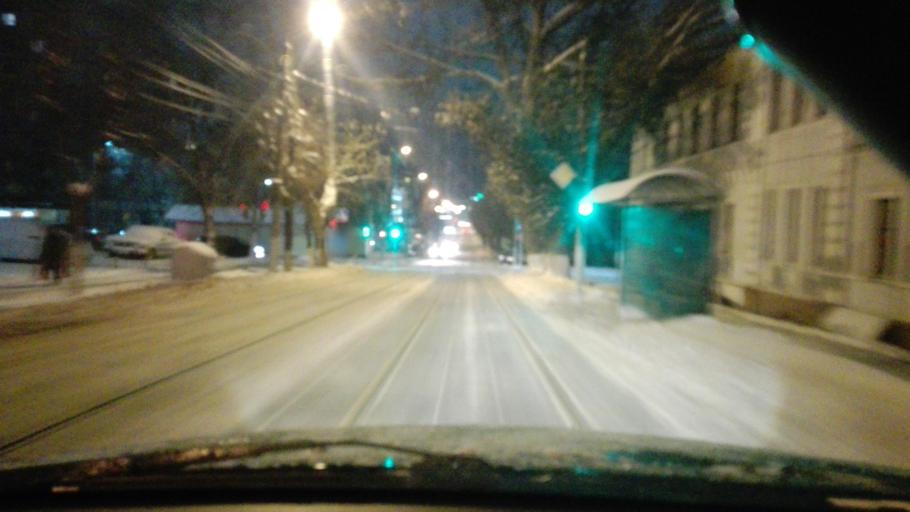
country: RU
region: Tula
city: Tula
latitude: 54.1895
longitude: 37.6098
